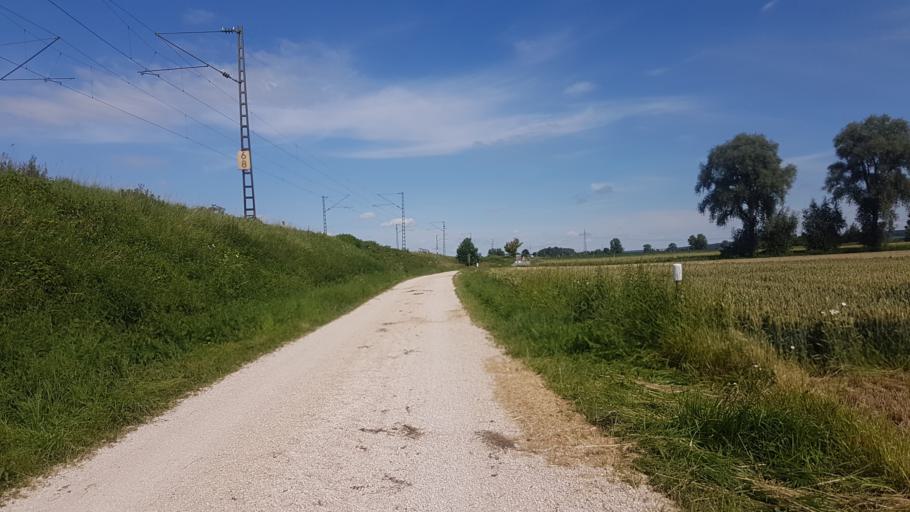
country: DE
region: Bavaria
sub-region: Regierungsbezirk Mittelfranken
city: Markt Berolzheim
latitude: 49.0069
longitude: 10.8608
